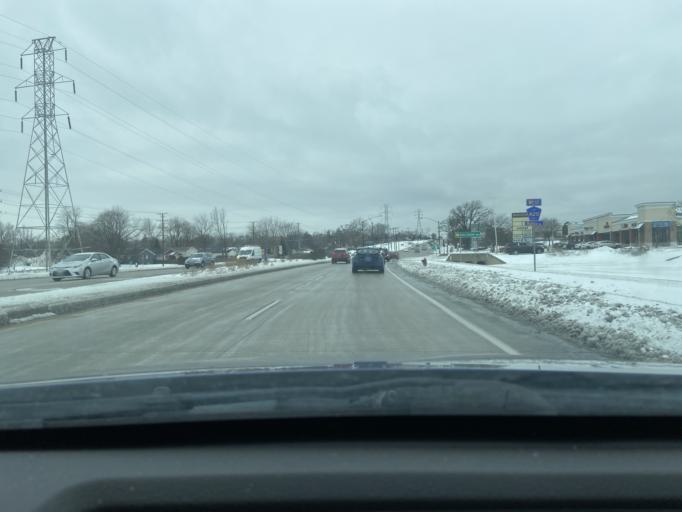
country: US
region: Illinois
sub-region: Lake County
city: Venetian Village
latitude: 42.3793
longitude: -88.0656
